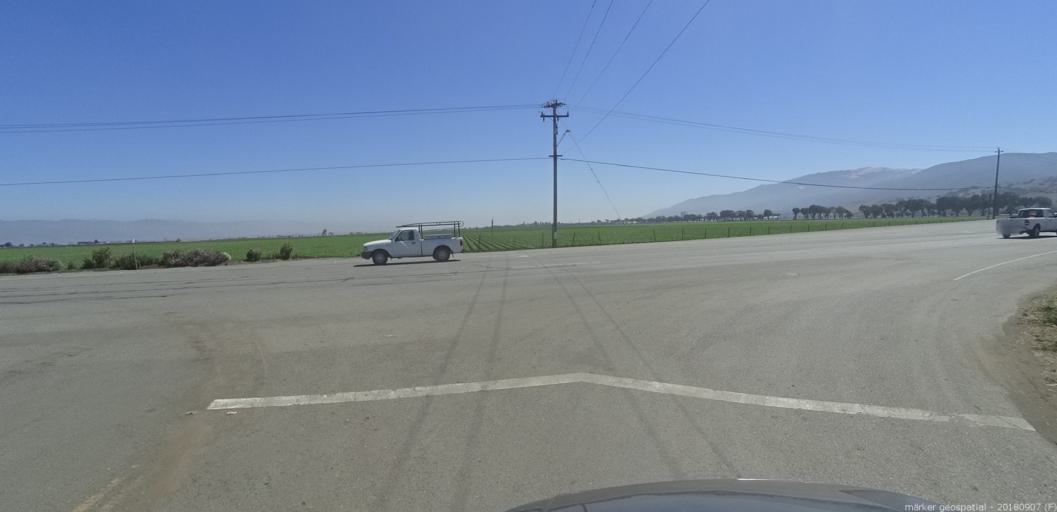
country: US
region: California
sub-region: Monterey County
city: Salinas
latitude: 36.6368
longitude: -121.6676
